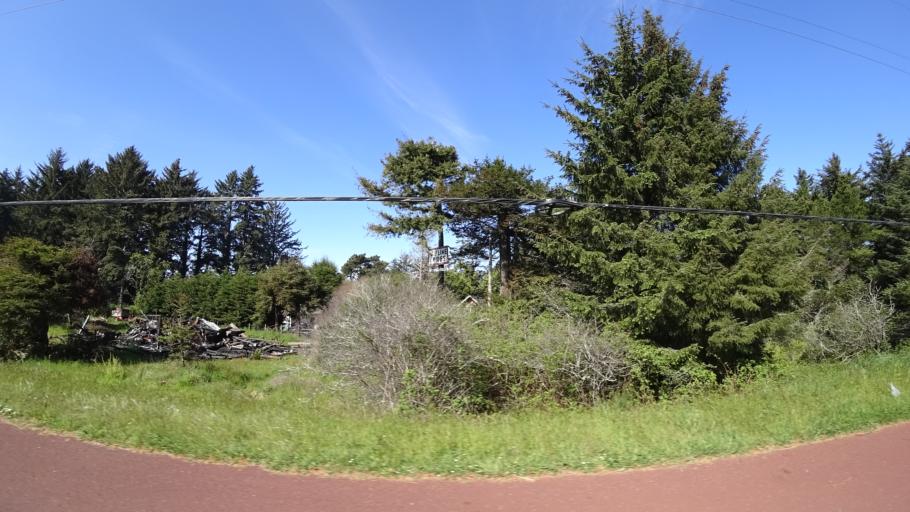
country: US
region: Oregon
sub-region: Curry County
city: Harbor
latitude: 41.9540
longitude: -124.2046
